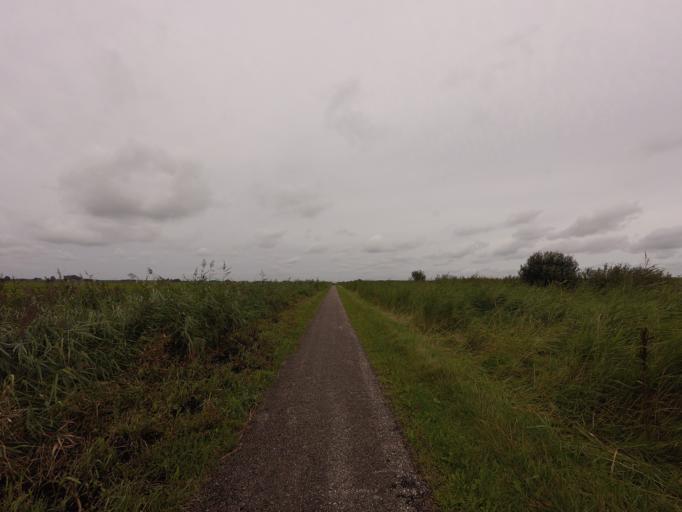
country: NL
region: Overijssel
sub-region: Gemeente Steenwijkerland
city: Blokzijl
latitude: 52.7741
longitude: 5.9095
